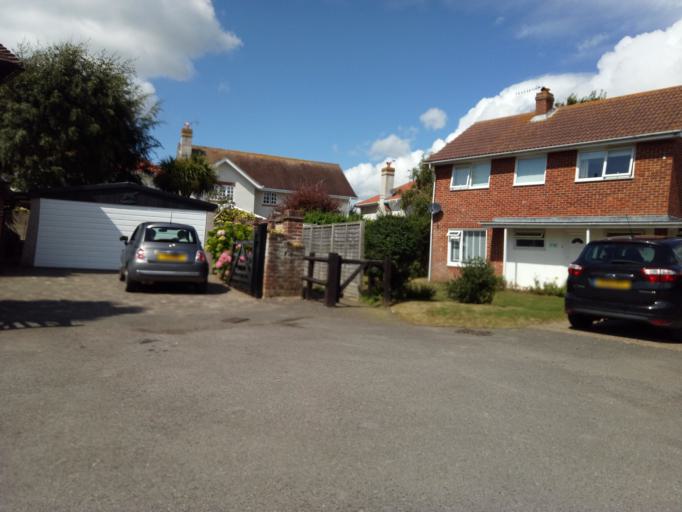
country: GB
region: England
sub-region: West Sussex
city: Barnham
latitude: 50.7905
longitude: -0.6332
